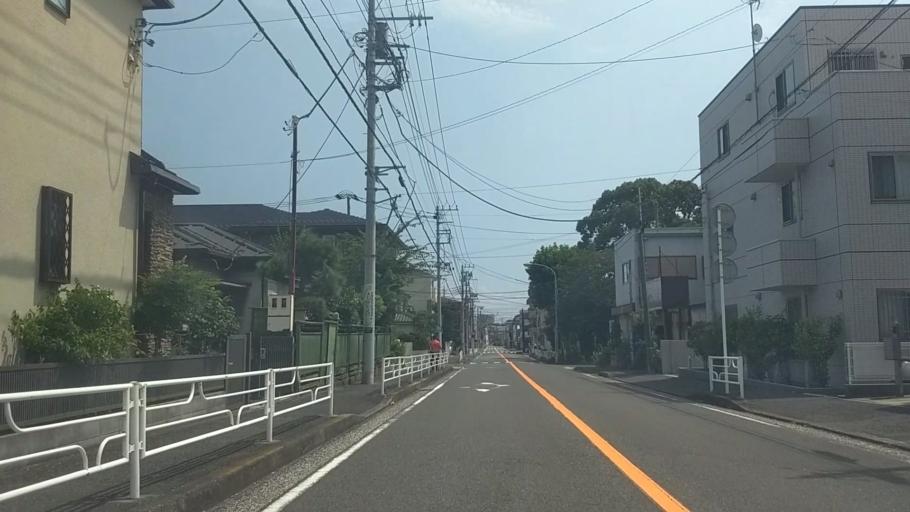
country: JP
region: Kanagawa
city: Yokohama
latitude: 35.4921
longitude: 139.6411
